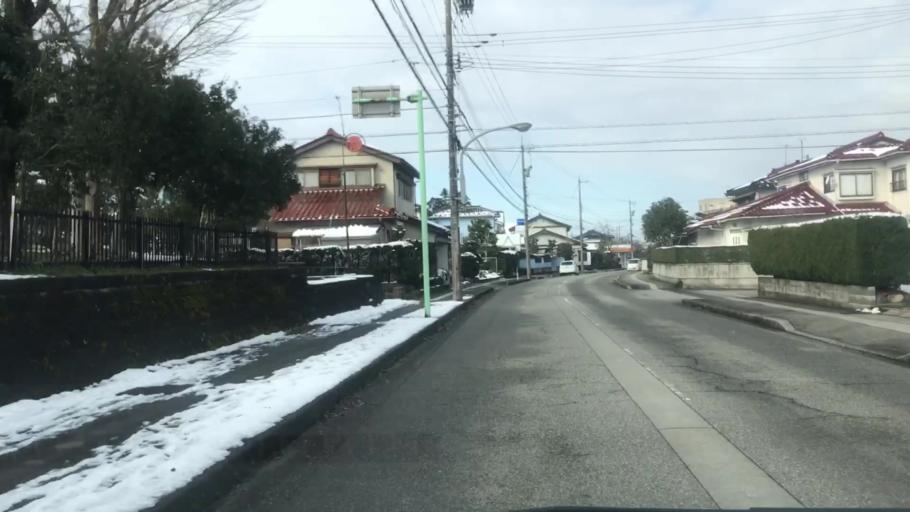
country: JP
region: Toyama
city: Toyama-shi
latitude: 36.6157
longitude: 137.2546
